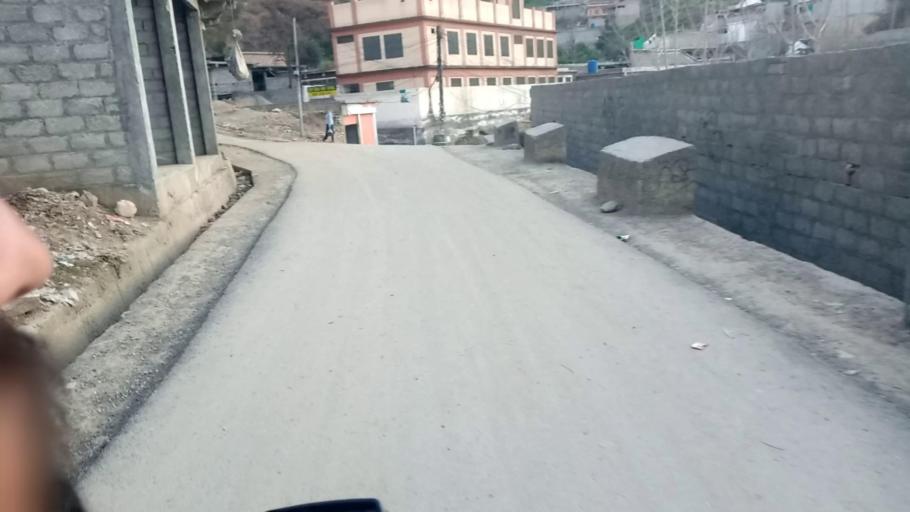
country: PK
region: Khyber Pakhtunkhwa
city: Saidu Sharif
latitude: 34.7370
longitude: 72.3448
